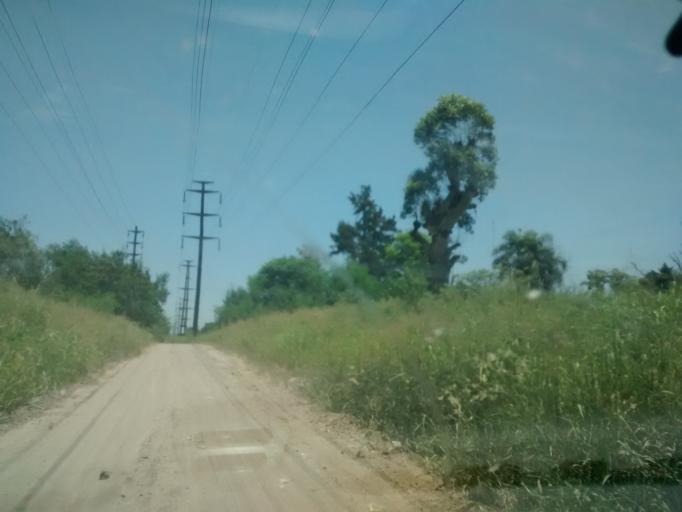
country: AR
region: Chaco
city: Fontana
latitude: -27.4134
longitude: -58.9860
